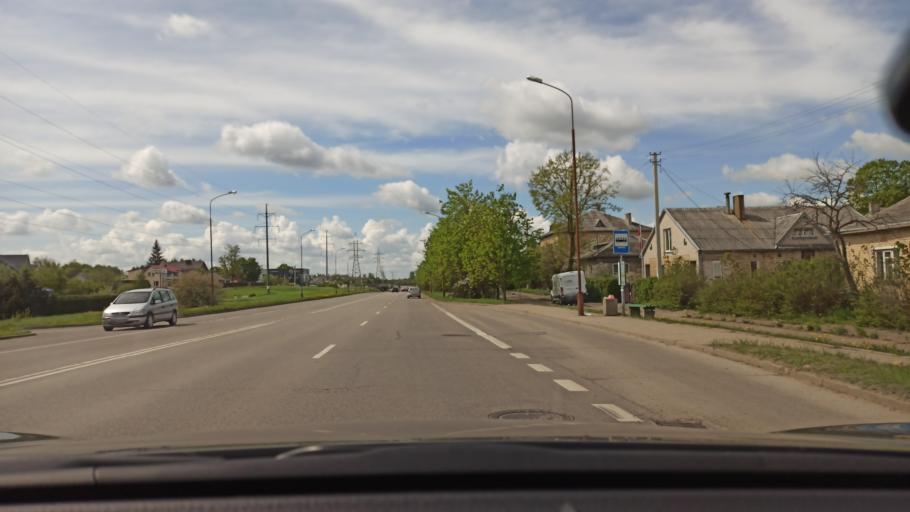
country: LT
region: Siauliu apskritis
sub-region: Siauliai
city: Siauliai
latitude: 55.9181
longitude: 23.3440
